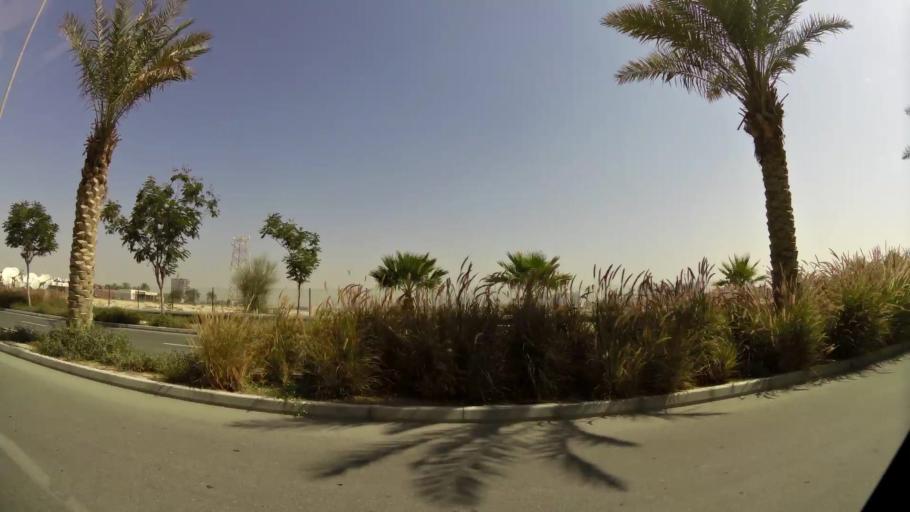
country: AE
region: Dubai
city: Dubai
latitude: 25.0229
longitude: 55.1448
